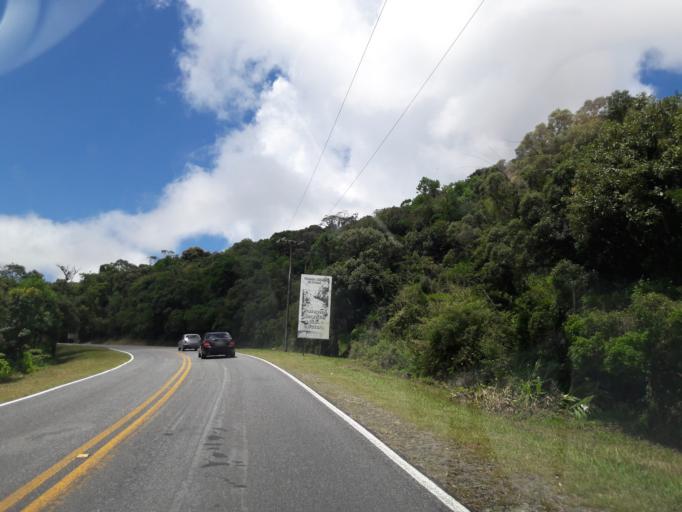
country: BR
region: Parana
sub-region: Campina Grande Do Sul
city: Campina Grande do Sul
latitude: -25.3324
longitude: -48.9109
